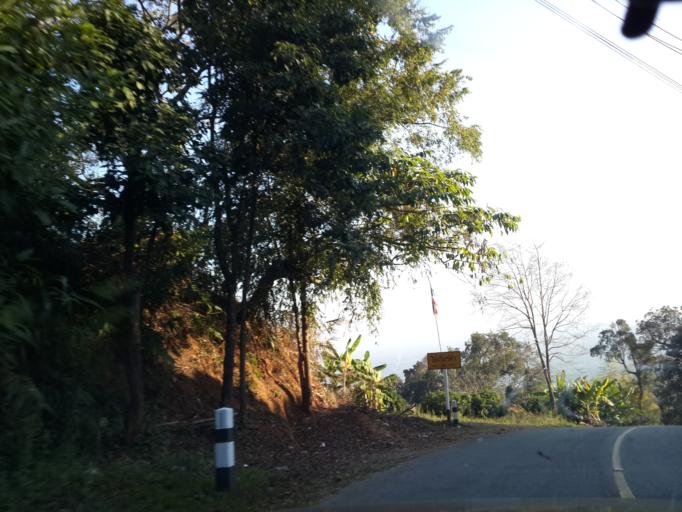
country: TH
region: Chiang Mai
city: Chai Prakan
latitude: 19.8347
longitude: 99.0981
